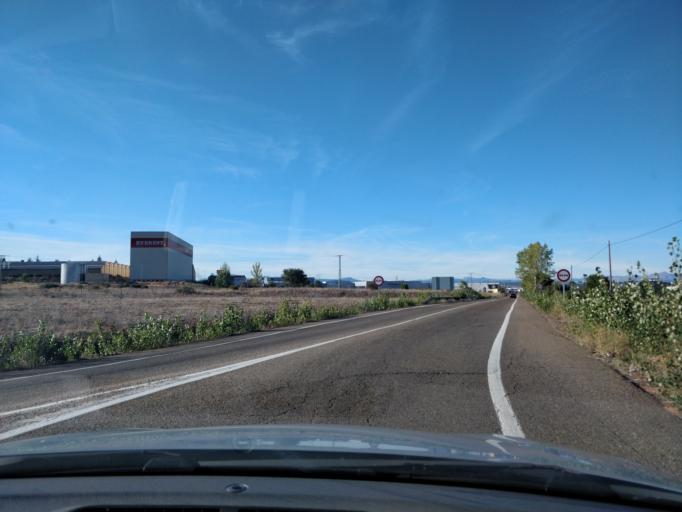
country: ES
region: Castille and Leon
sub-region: Provincia de Leon
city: San Andres del Rabanedo
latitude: 42.5832
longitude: -5.6196
